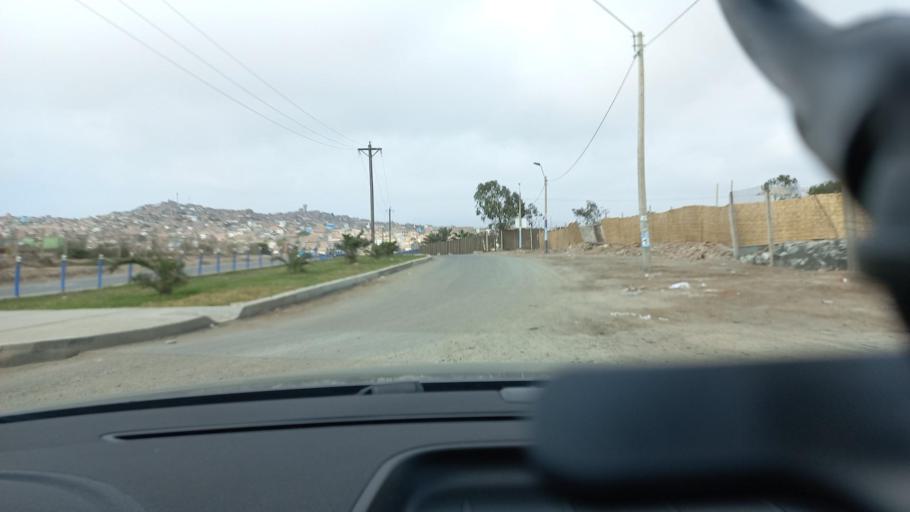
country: PE
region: Lima
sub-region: Lima
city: Surco
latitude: -12.2041
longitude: -76.9998
